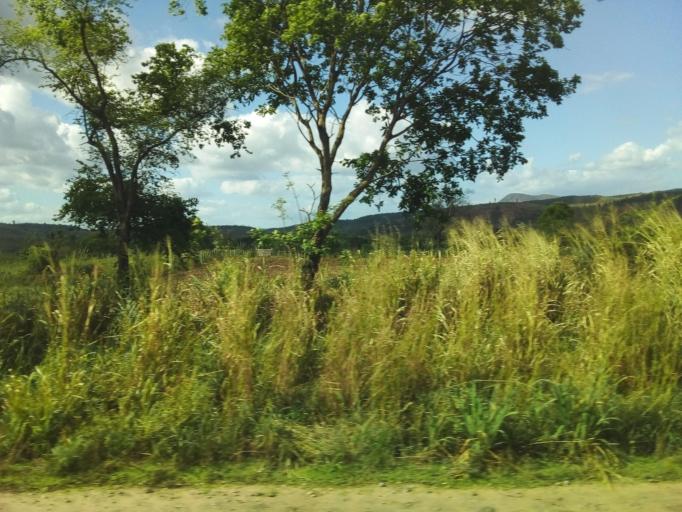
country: BR
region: Minas Gerais
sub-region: Conselheiro Pena
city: Conselheiro Pena
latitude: -18.9834
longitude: -41.6089
